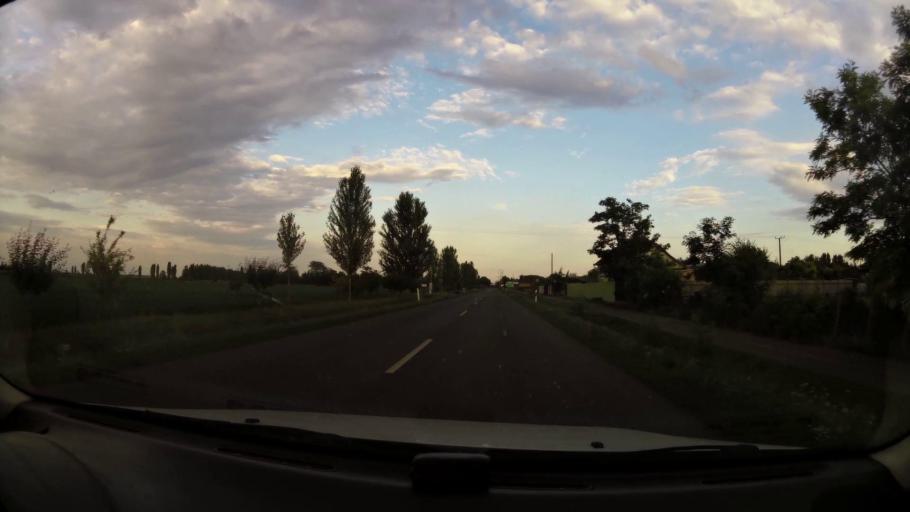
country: HU
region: Pest
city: Ujszilvas
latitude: 47.2802
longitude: 19.9210
